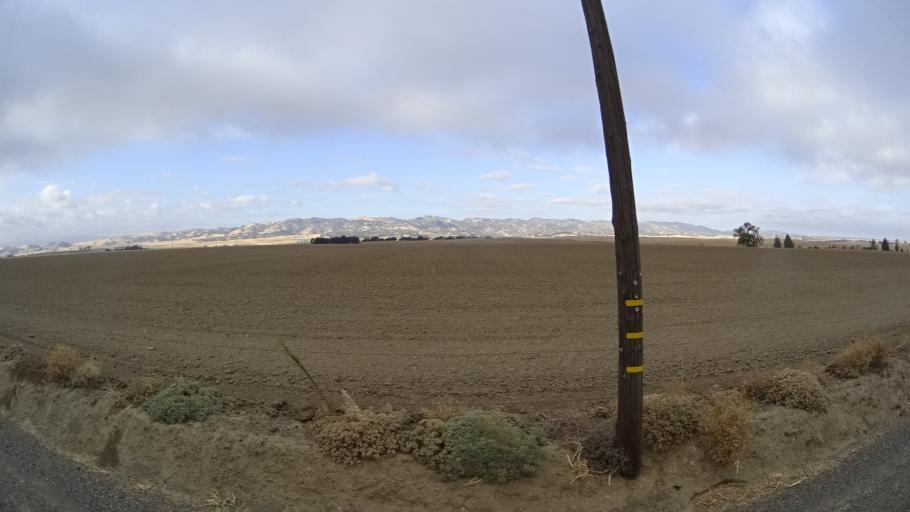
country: US
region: California
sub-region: Yolo County
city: Esparto
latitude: 38.7986
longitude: -122.0435
